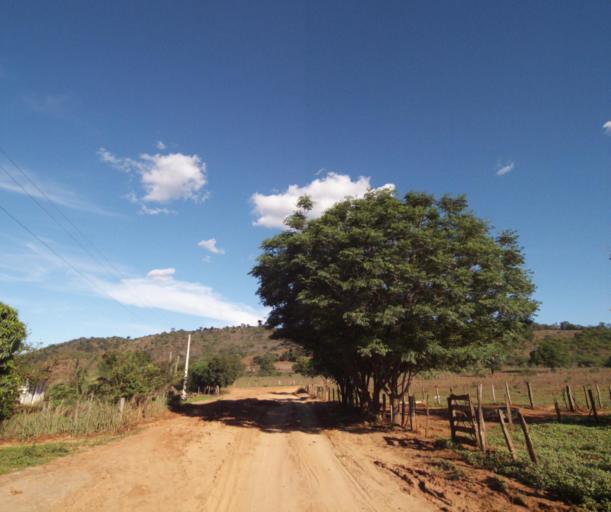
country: BR
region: Bahia
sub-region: Carinhanha
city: Carinhanha
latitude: -14.2821
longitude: -44.4701
